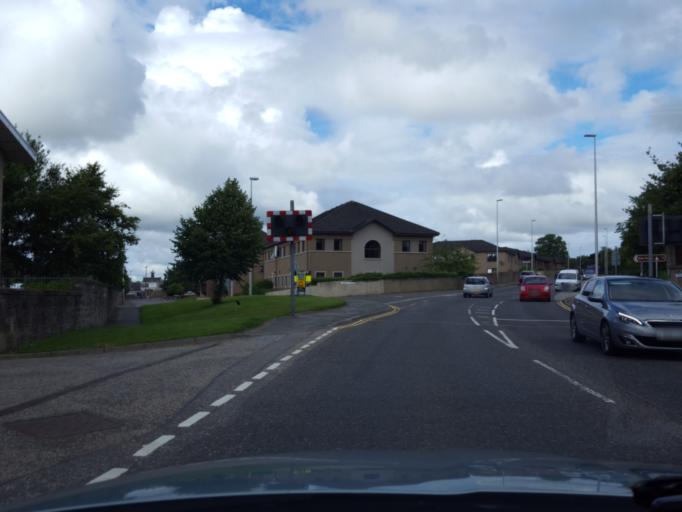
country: GB
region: Scotland
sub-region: Moray
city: Elgin
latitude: 57.6433
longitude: -3.3122
